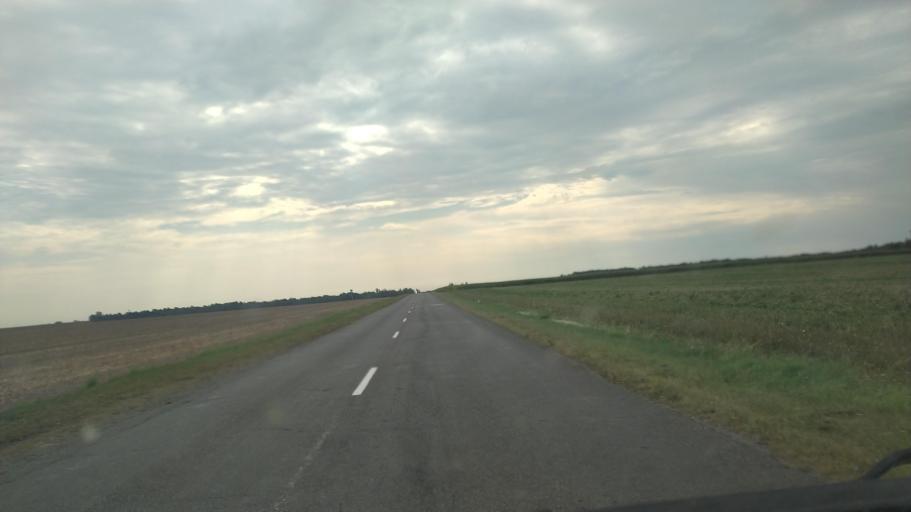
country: BY
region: Brest
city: Byaroza
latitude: 52.5719
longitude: 24.8852
